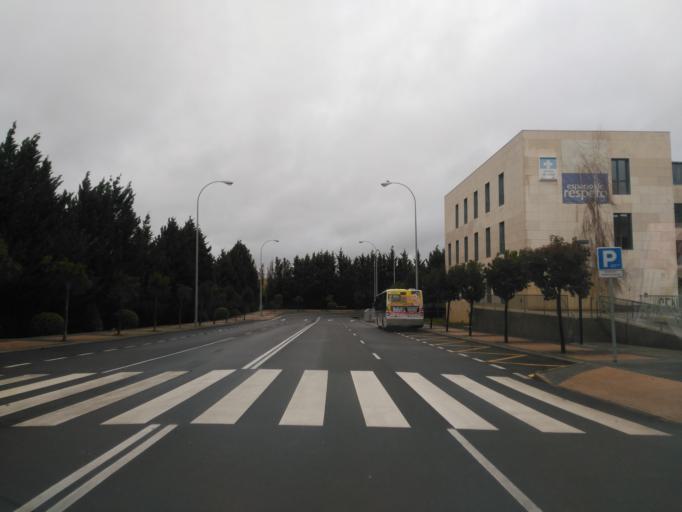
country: ES
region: Castille and Leon
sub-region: Provincia de Salamanca
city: Salamanca
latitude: 40.9839
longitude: -5.6672
